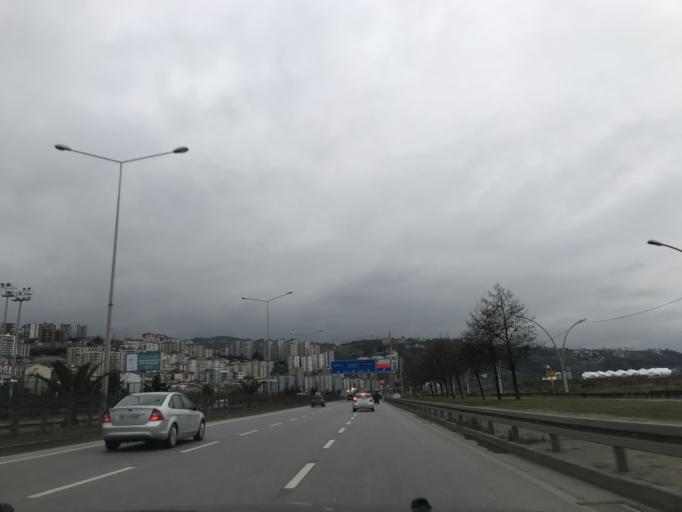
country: TR
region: Trabzon
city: Trabzon
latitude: 40.9972
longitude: 39.6704
